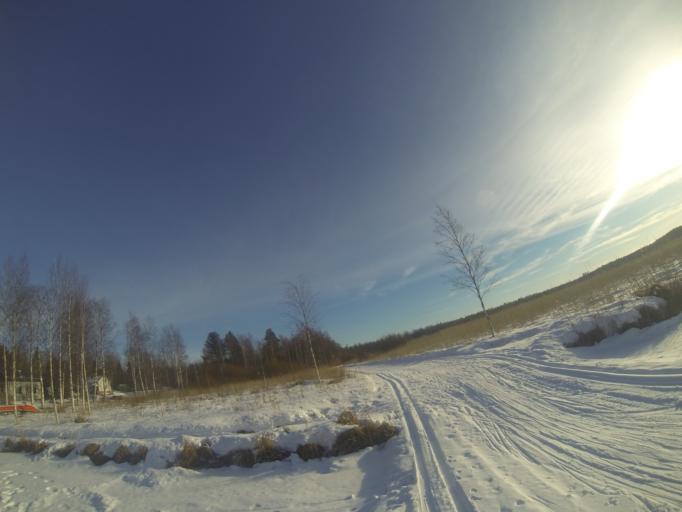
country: FI
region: Southern Savonia
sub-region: Savonlinna
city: Savonlinna
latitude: 61.9127
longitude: 28.9159
